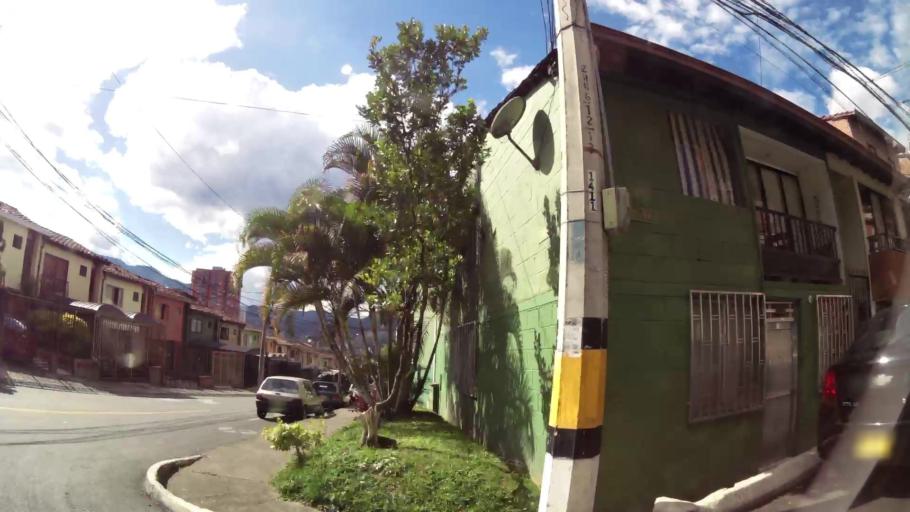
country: CO
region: Antioquia
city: Sabaneta
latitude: 6.1551
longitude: -75.6059
